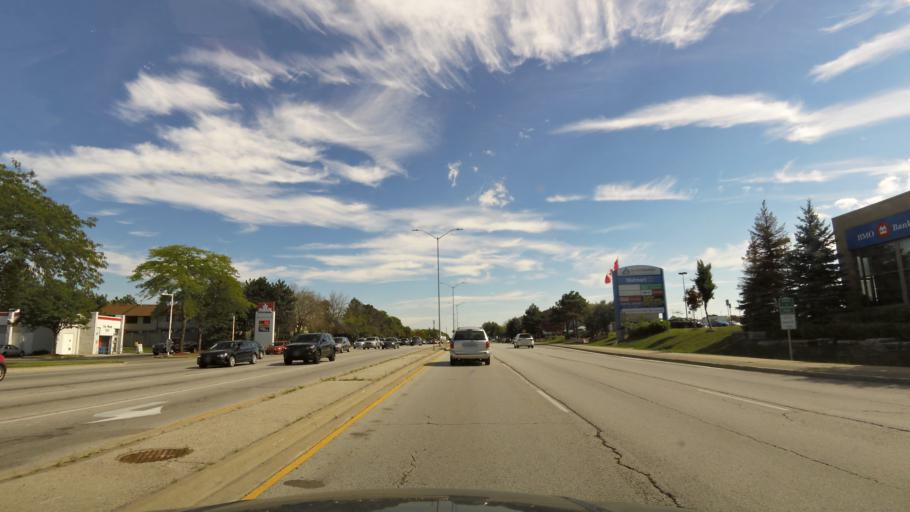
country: CA
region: Ontario
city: Mississauga
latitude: 43.5463
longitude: -79.6832
